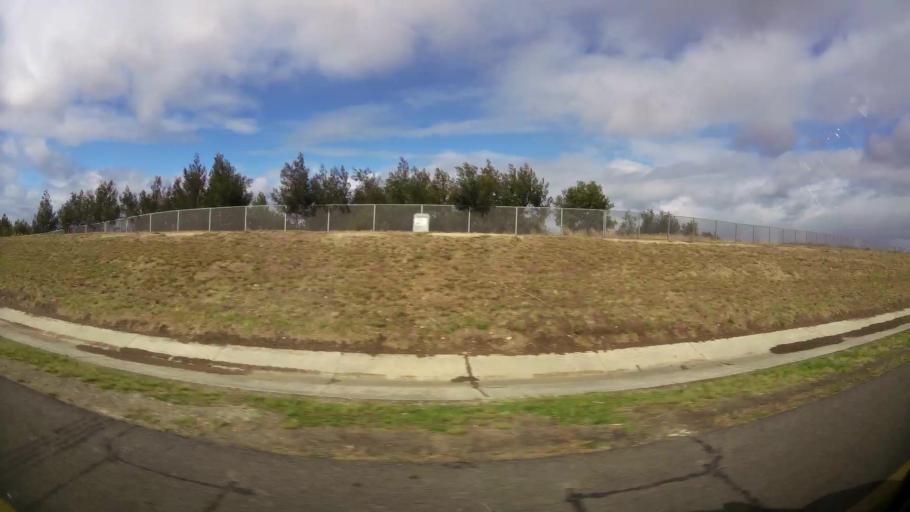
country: ZA
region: Western Cape
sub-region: Eden District Municipality
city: George
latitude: -33.9981
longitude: 22.4480
